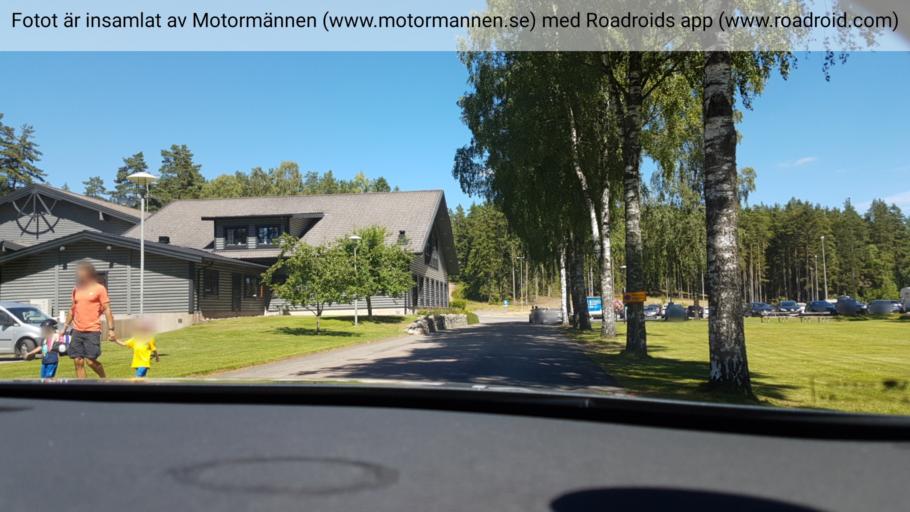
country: SE
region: Joenkoeping
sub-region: Gnosjo Kommun
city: Gnosjoe
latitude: 57.4363
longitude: 13.6234
